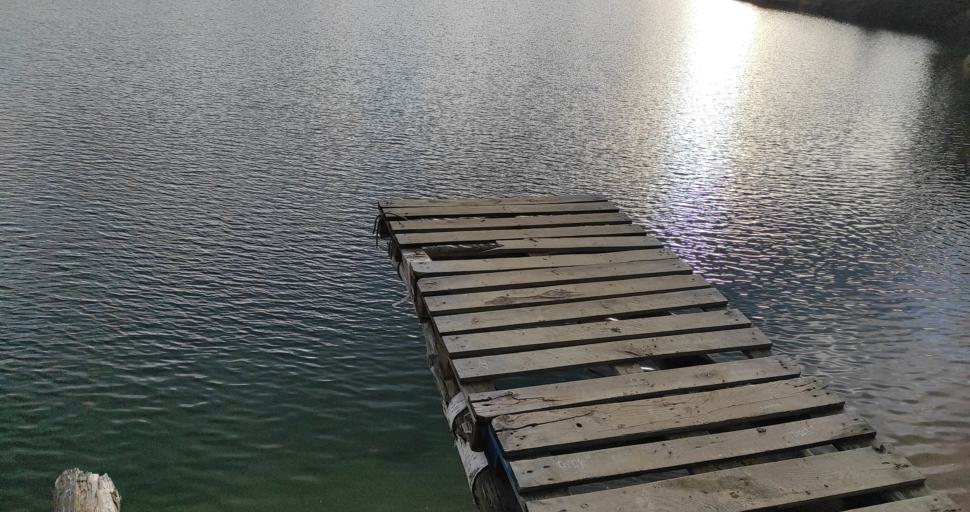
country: RU
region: Leningrad
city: Toksovo
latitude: 60.1199
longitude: 30.5449
